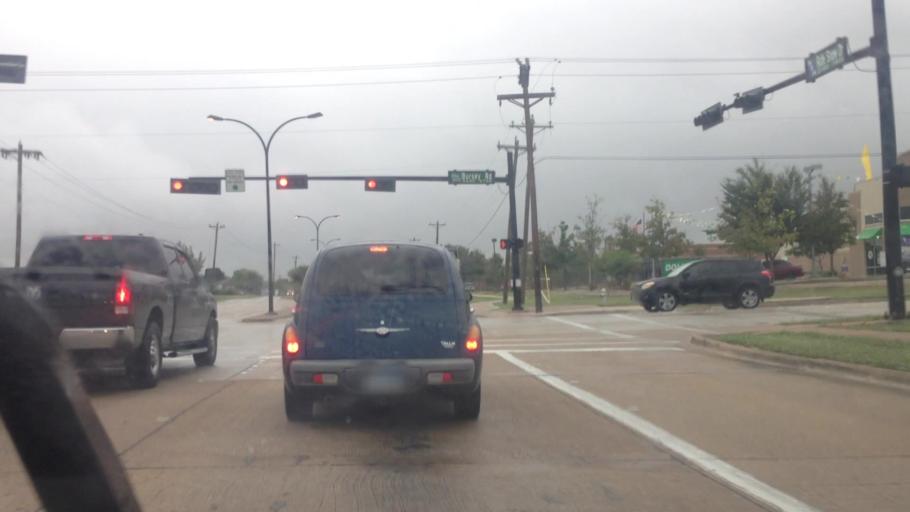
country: US
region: Texas
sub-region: Tarrant County
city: Watauga
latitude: 32.8921
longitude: -97.2385
